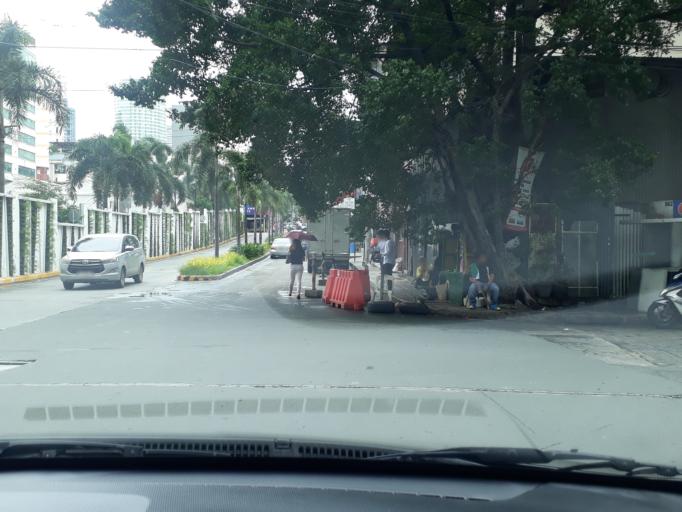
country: PH
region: Metro Manila
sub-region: Makati City
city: Makati City
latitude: 14.5651
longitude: 121.0291
